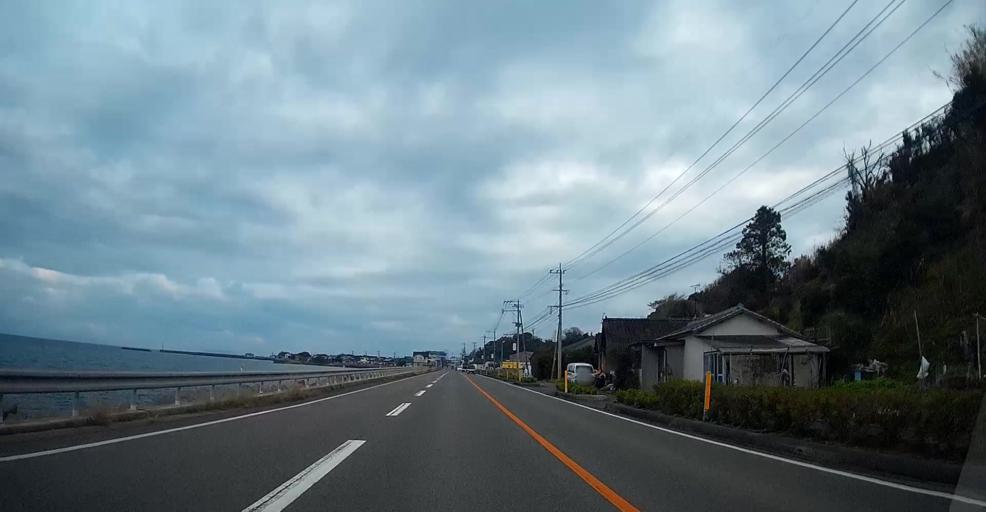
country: JP
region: Kumamoto
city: Hondo
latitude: 32.4689
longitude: 130.2490
